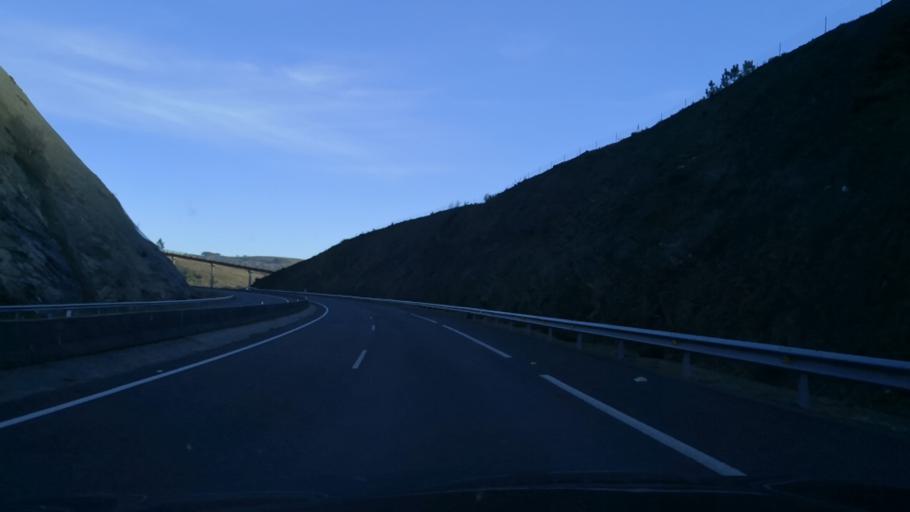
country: ES
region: Galicia
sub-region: Provincia de Pontevedra
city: Dozon
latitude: 42.5909
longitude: -8.0838
